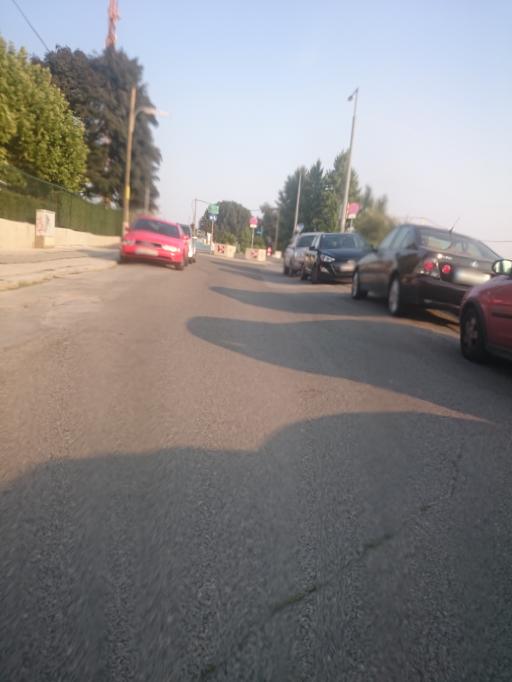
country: AT
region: Vienna
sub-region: Wien Stadt
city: Vienna
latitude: 48.2391
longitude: 16.4286
